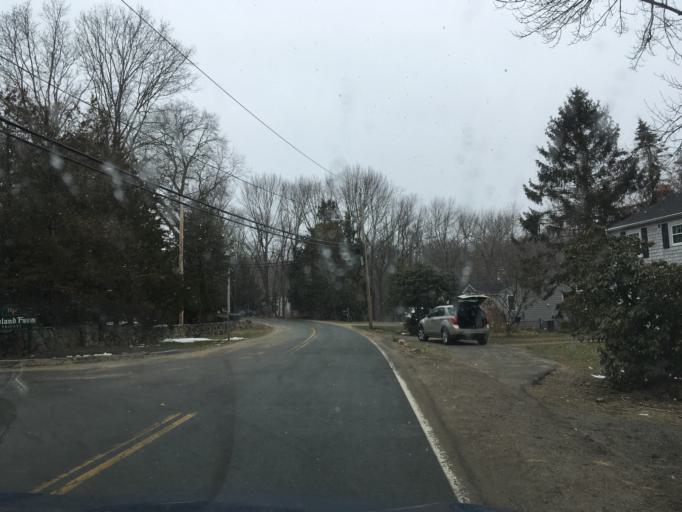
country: US
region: Rhode Island
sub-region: Kent County
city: East Greenwich
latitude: 41.6616
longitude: -71.4725
